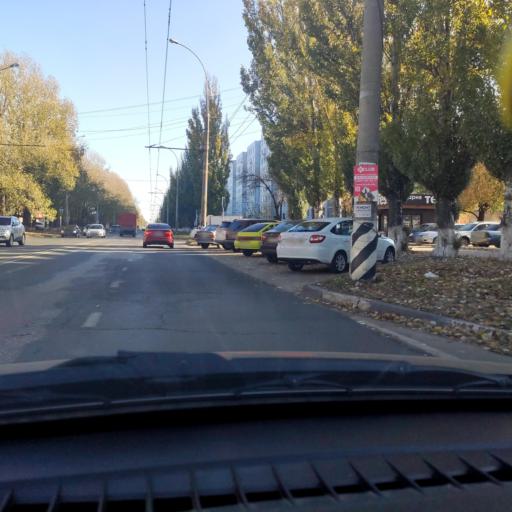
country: RU
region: Samara
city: Tol'yatti
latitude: 53.5371
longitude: 49.2891
